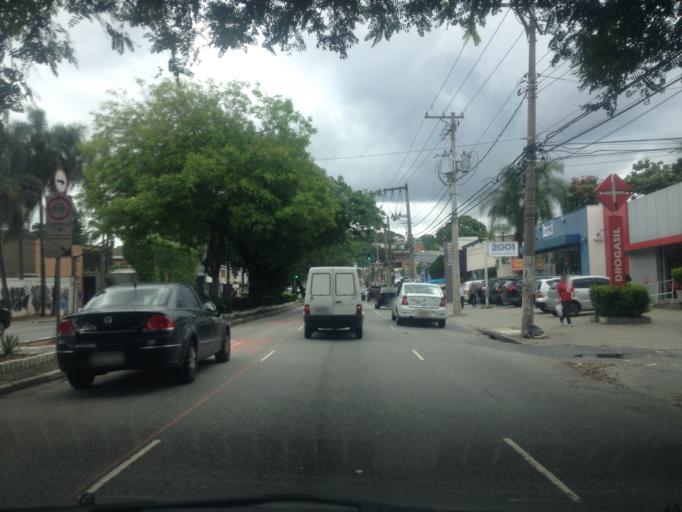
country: BR
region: Sao Paulo
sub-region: Sao Paulo
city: Sao Paulo
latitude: -23.5864
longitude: -46.6950
